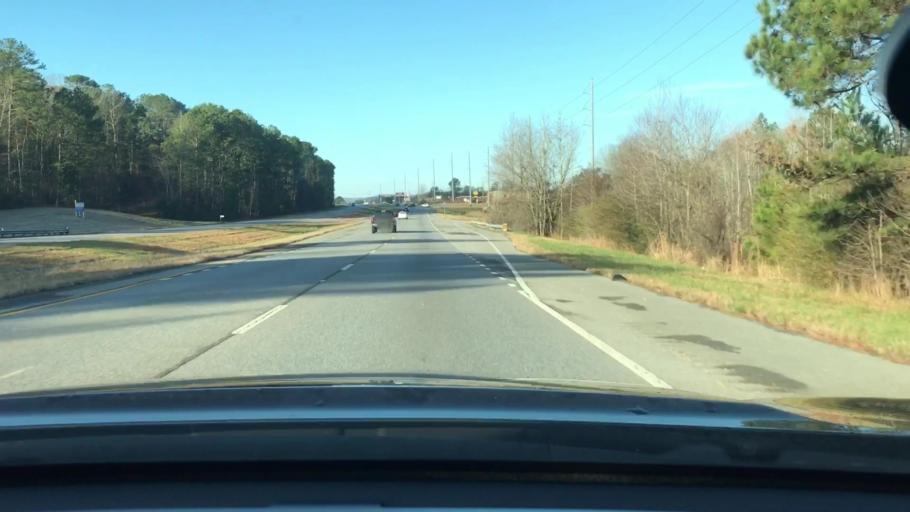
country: US
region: Alabama
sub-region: Shelby County
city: Chelsea
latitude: 33.3511
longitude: -86.6039
